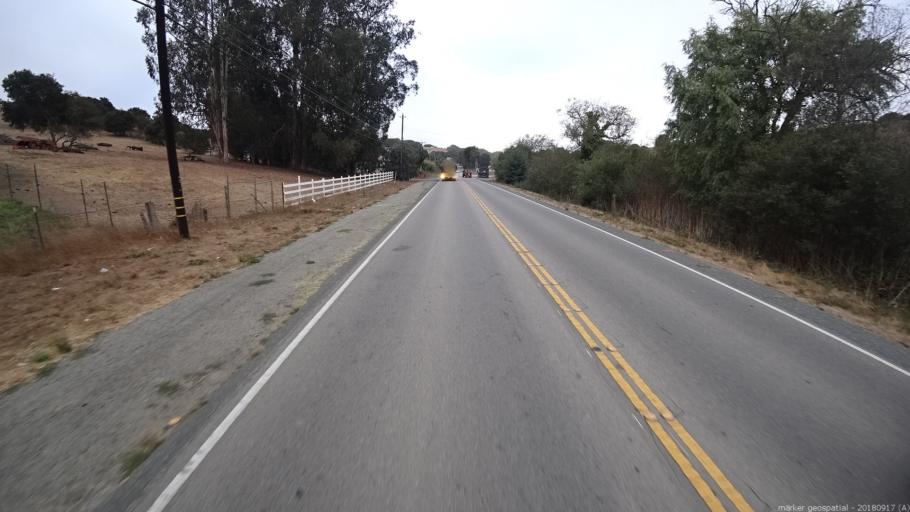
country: US
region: California
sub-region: Monterey County
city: Prunedale
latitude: 36.7956
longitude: -121.7052
